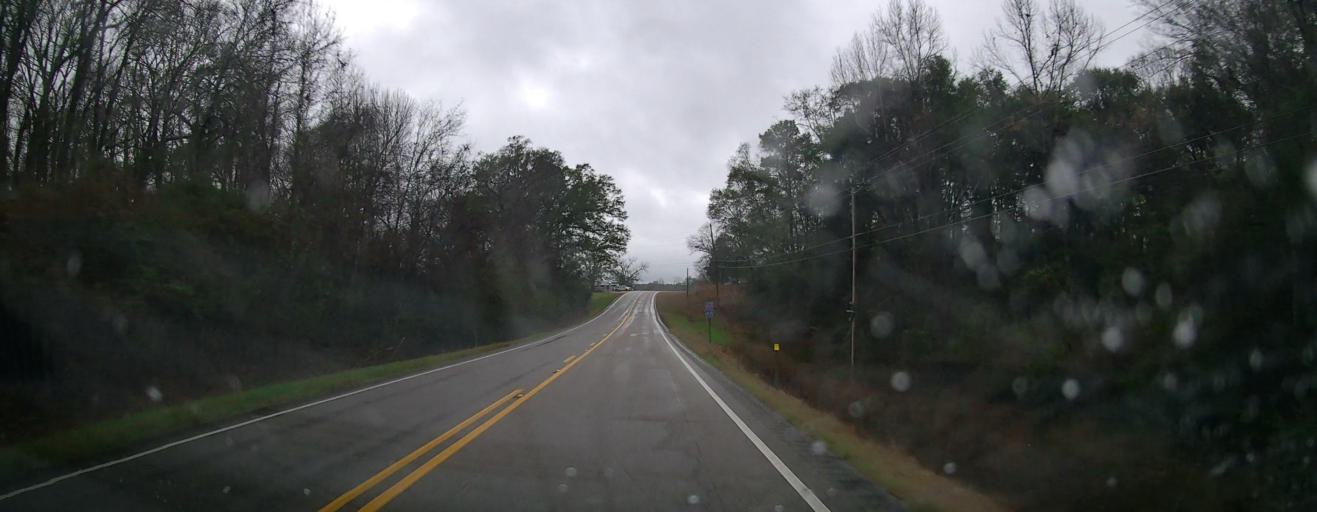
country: US
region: Alabama
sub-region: Autauga County
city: Pine Level
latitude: 32.5317
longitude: -86.6362
